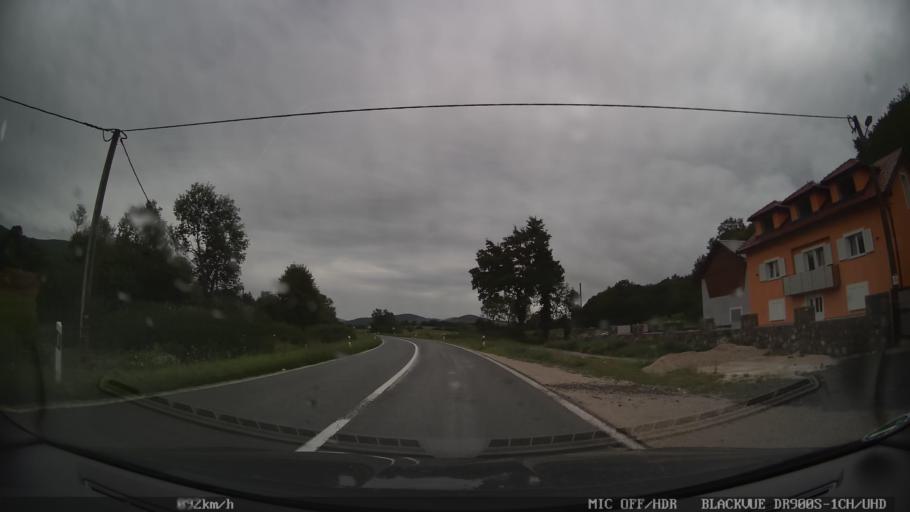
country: HR
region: Licko-Senjska
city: Brinje
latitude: 44.9539
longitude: 15.1018
